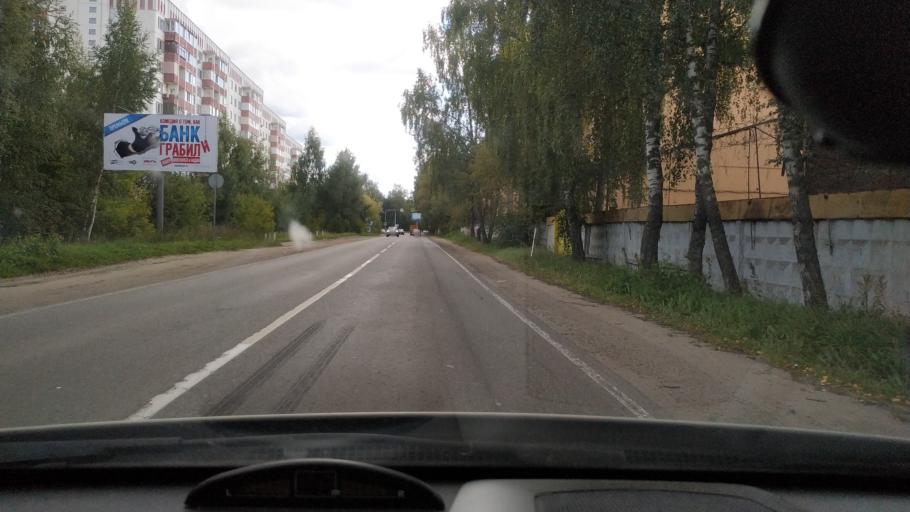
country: RU
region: Moskovskaya
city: Chornaya
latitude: 55.7618
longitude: 38.0743
